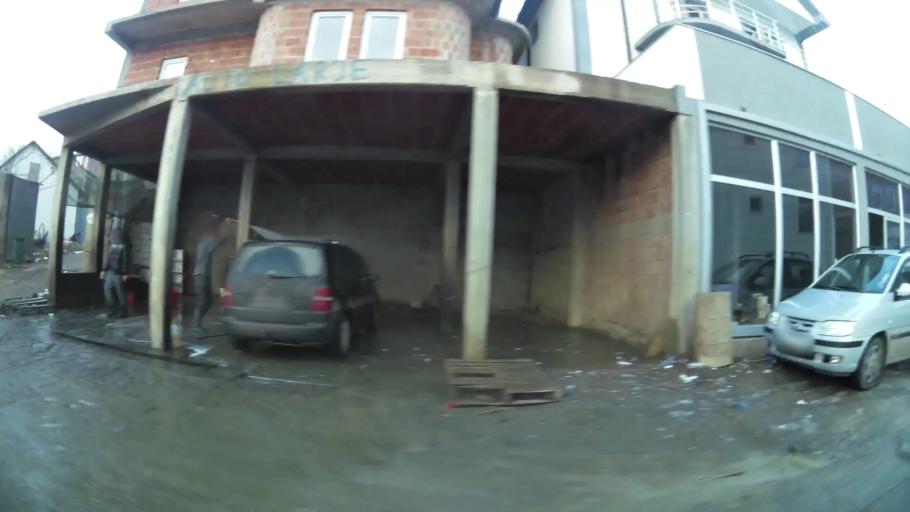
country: MK
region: Aracinovo
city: Arachinovo
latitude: 42.0272
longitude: 21.5627
